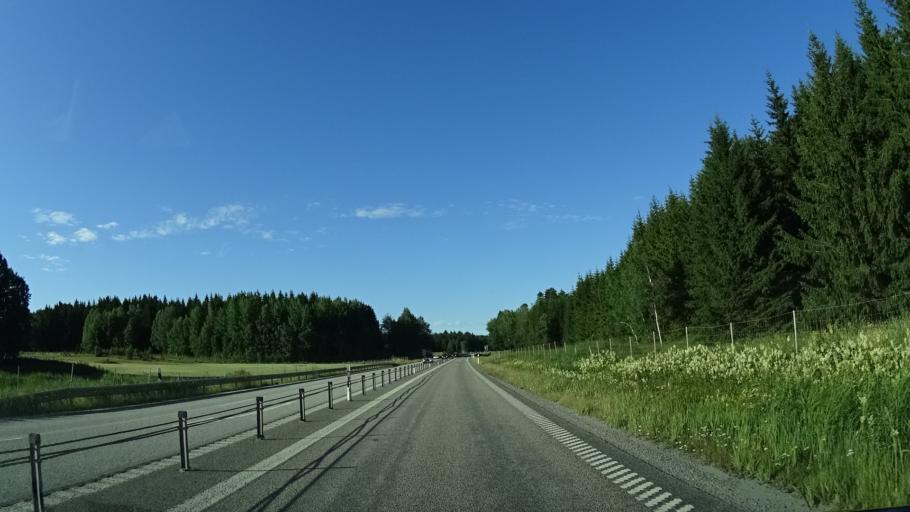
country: SE
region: Stockholm
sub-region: Vallentuna Kommun
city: Vallentuna
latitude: 59.5178
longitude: 18.1796
